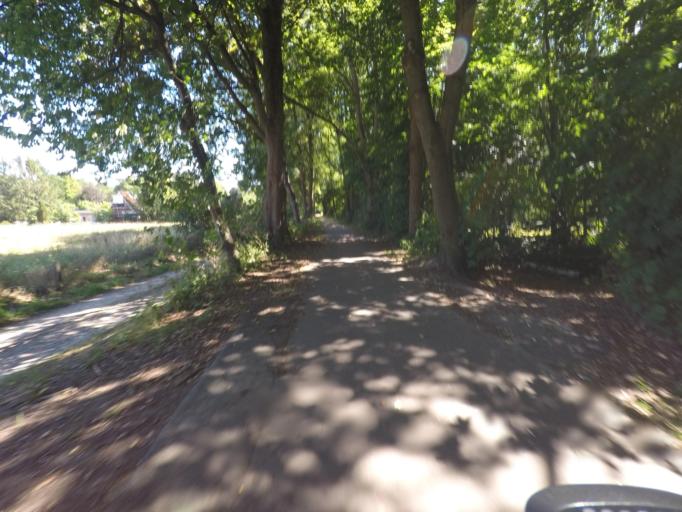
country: DE
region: Schleswig-Holstein
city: Lutjensee
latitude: 53.6378
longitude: 10.3759
